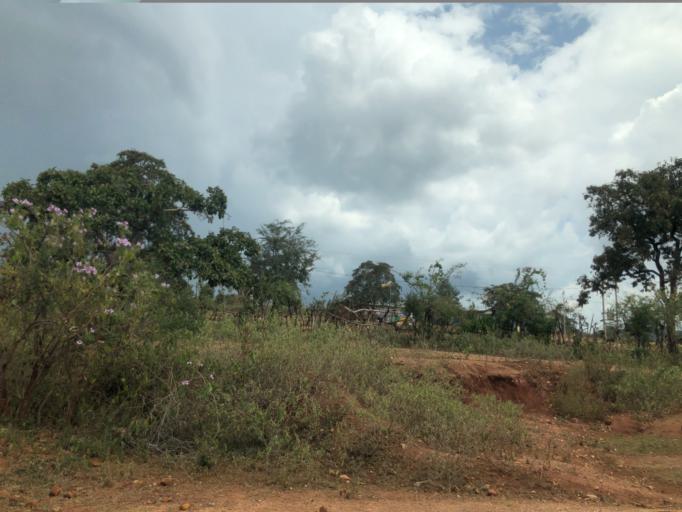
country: ET
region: Southern Nations, Nationalities, and People's Region
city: Jinka
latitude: 5.5981
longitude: 36.6933
